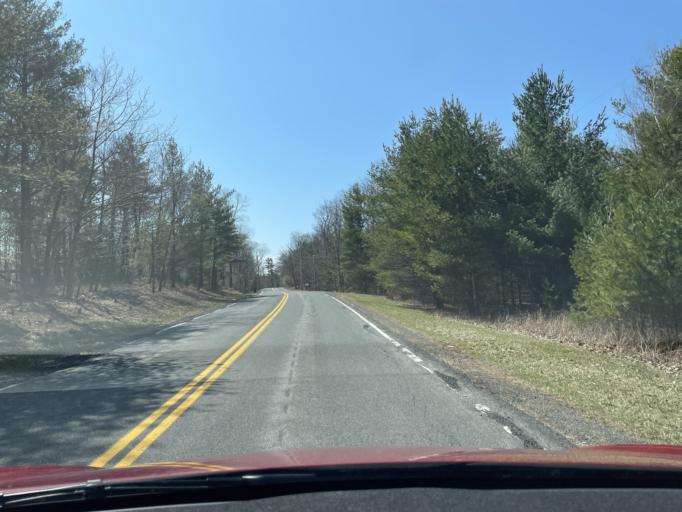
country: US
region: New York
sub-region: Ulster County
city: Manorville
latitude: 42.0856
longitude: -74.0613
